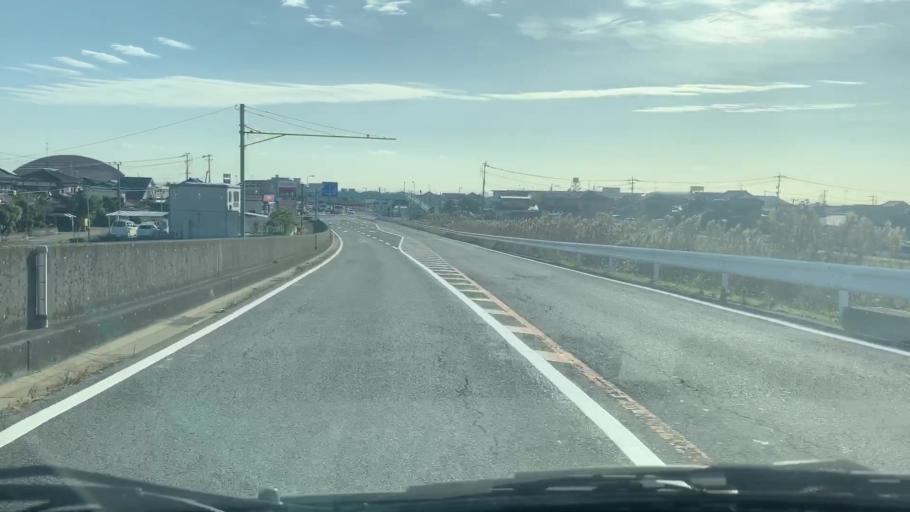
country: JP
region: Saga Prefecture
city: Kashima
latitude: 33.2187
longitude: 130.1549
